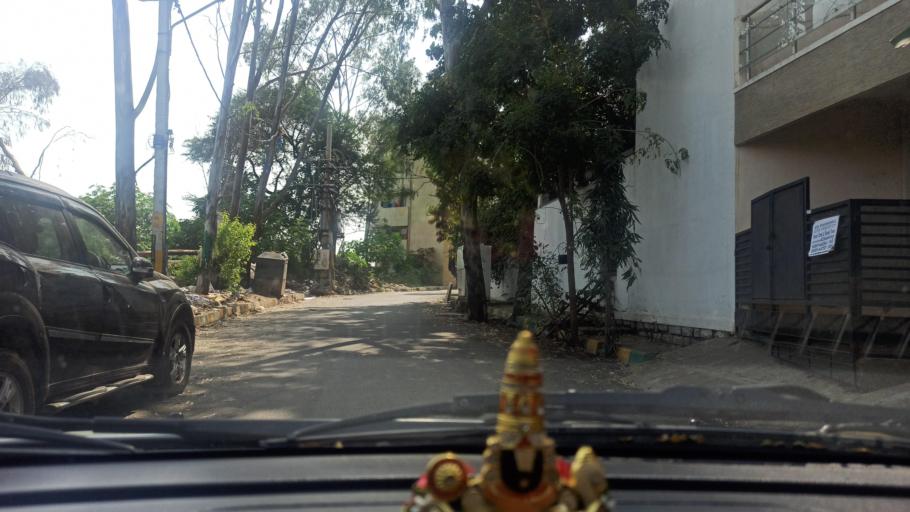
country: IN
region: Karnataka
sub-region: Bangalore Urban
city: Bangalore
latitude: 13.0202
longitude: 77.6622
